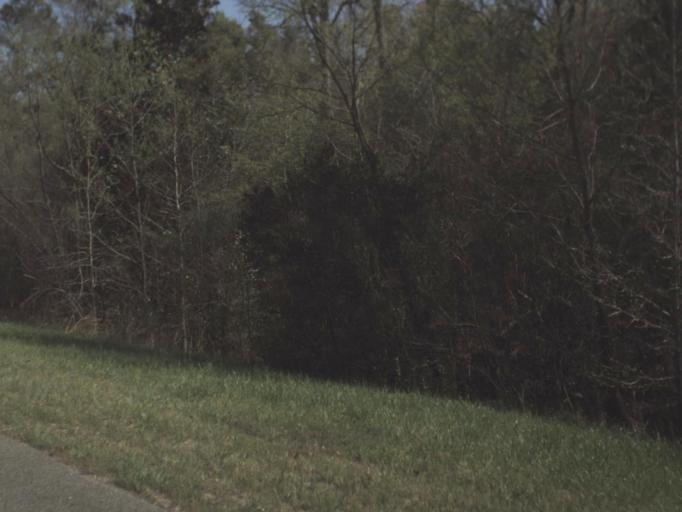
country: US
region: Florida
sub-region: Gadsden County
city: Quincy
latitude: 30.3878
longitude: -84.6699
